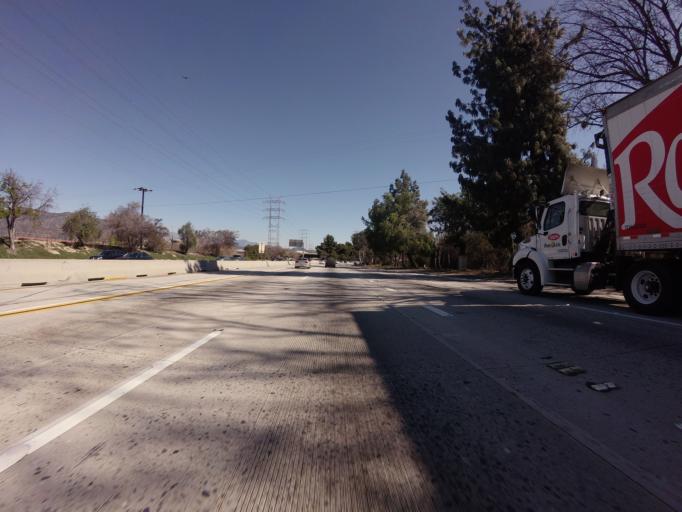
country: US
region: California
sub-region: Los Angeles County
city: North Glendale
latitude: 34.1552
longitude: -118.2930
